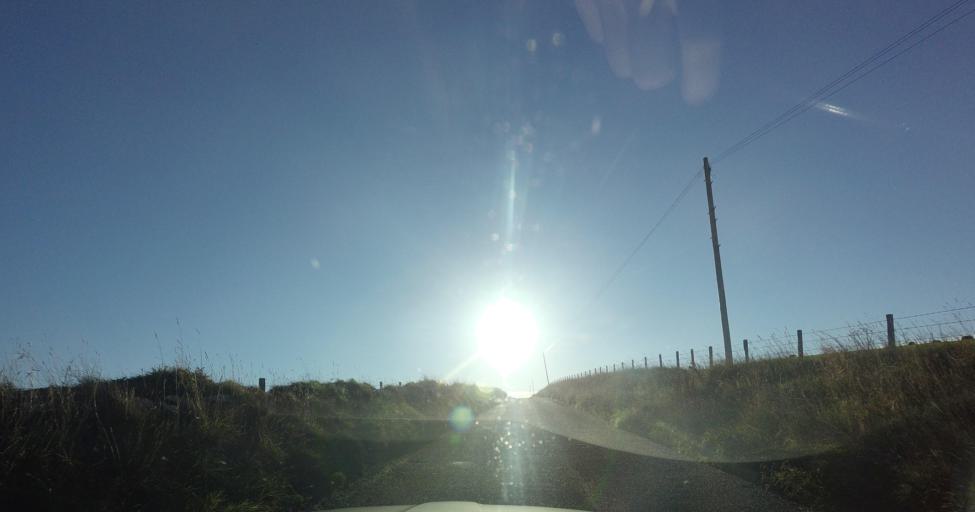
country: GB
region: Scotland
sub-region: Aberdeenshire
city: Rosehearty
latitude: 57.6789
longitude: -2.2651
